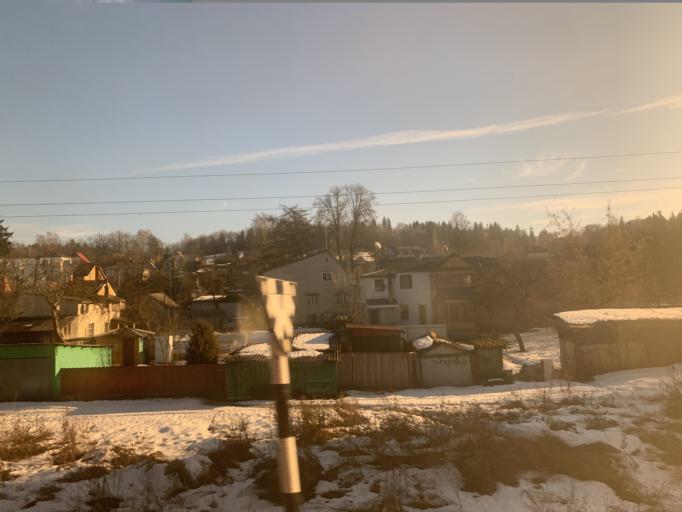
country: LT
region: Vilnius County
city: Rasos
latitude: 54.6788
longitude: 25.3556
